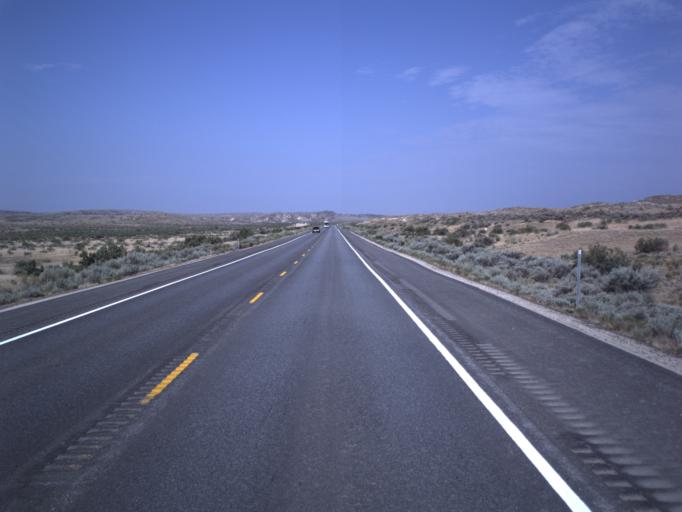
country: US
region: Colorado
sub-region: Rio Blanco County
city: Rangely
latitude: 40.2850
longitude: -109.1196
